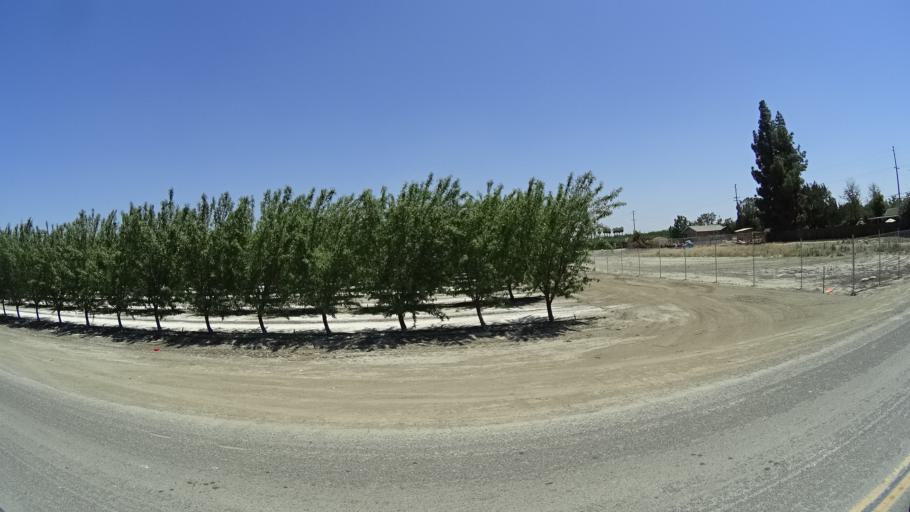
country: US
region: California
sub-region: Kings County
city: Armona
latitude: 36.3147
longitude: -119.7270
